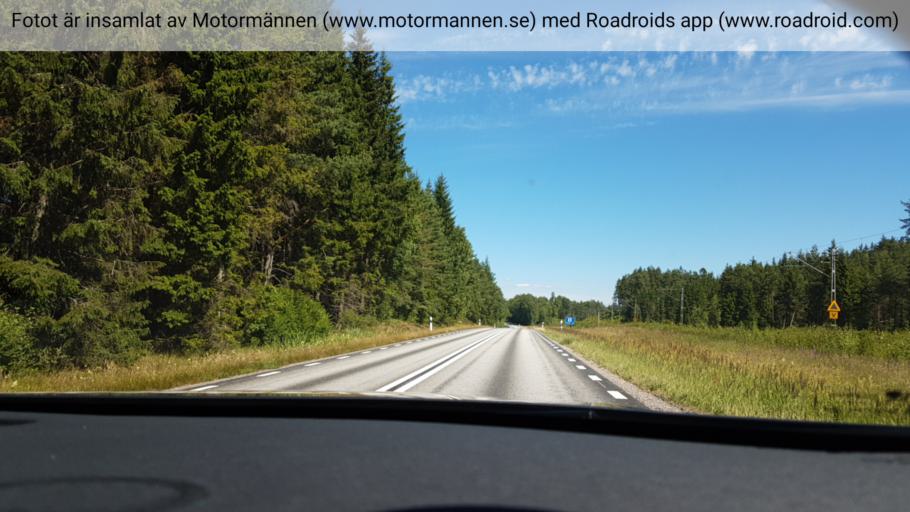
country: SE
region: Joenkoeping
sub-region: Gnosjo Kommun
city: Hillerstorp
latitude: 57.3202
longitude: 13.8511
